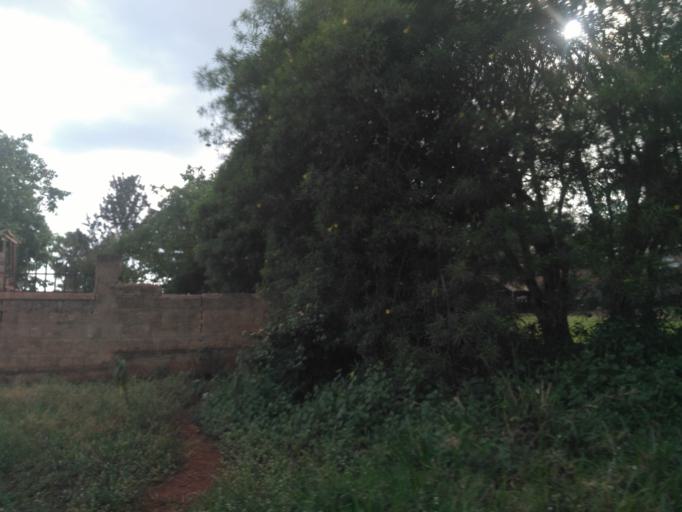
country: UG
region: Eastern Region
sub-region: Jinja District
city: Jinja
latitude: 0.4216
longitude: 33.2124
